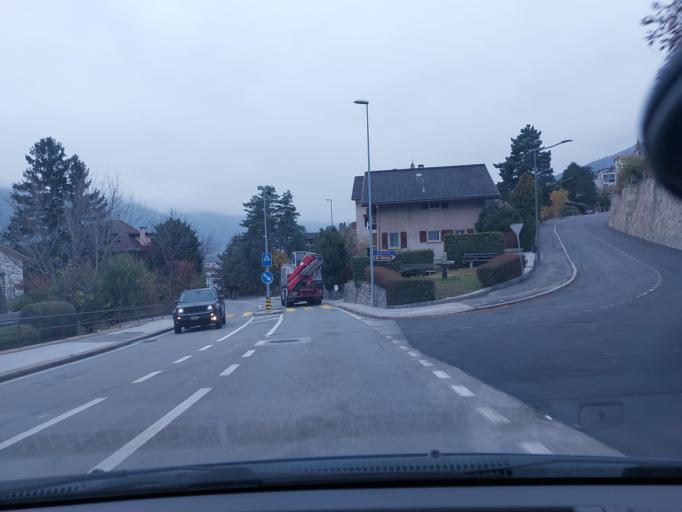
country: CH
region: Valais
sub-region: Sierre District
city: Veyras
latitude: 46.2983
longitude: 7.5347
